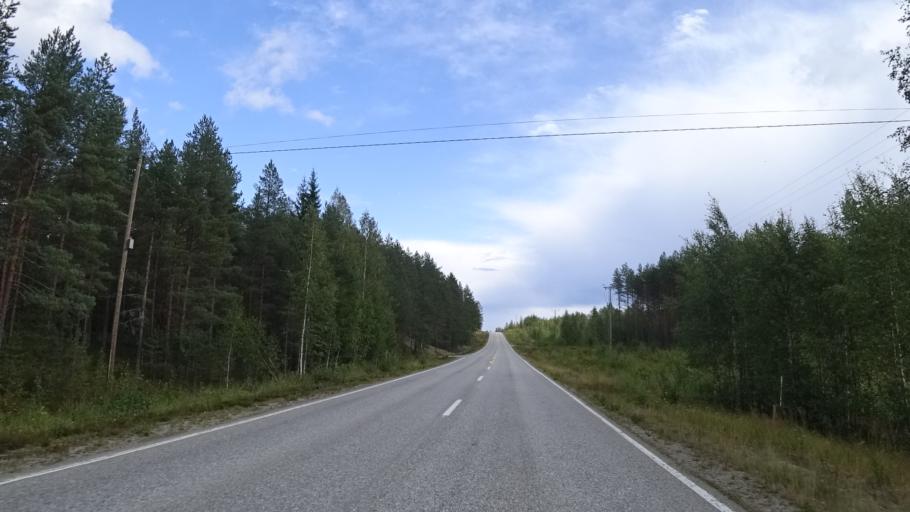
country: FI
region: North Karelia
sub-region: Joensuu
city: Ilomantsi
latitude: 62.6429
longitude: 31.0506
